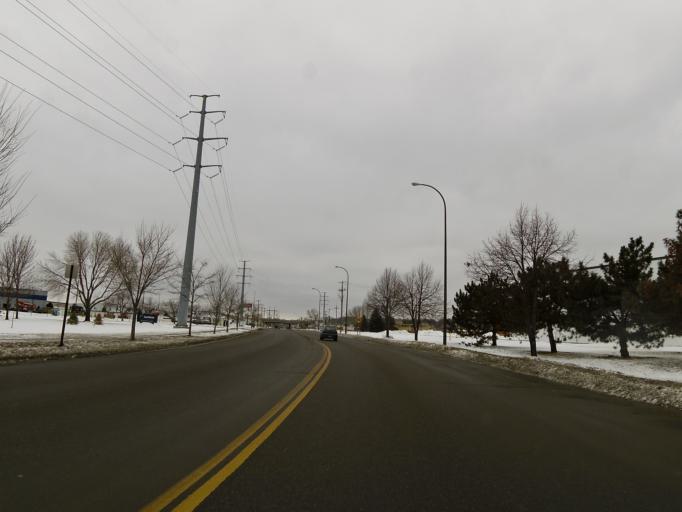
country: US
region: Minnesota
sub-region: Dakota County
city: South Saint Paul
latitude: 44.8860
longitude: -93.0244
